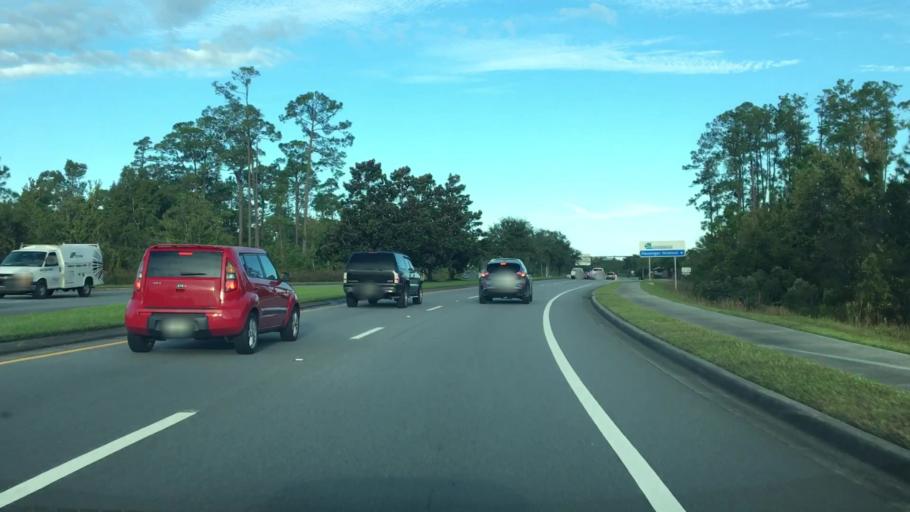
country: US
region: Florida
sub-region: Seminole County
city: Midway
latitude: 28.7573
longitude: -81.2400
